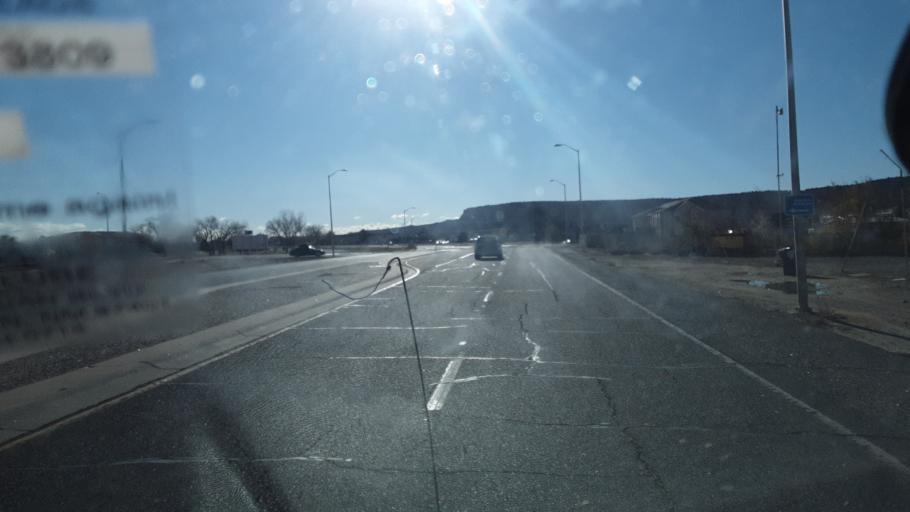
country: US
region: New Mexico
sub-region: San Juan County
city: Farmington
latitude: 36.7223
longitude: -108.1864
